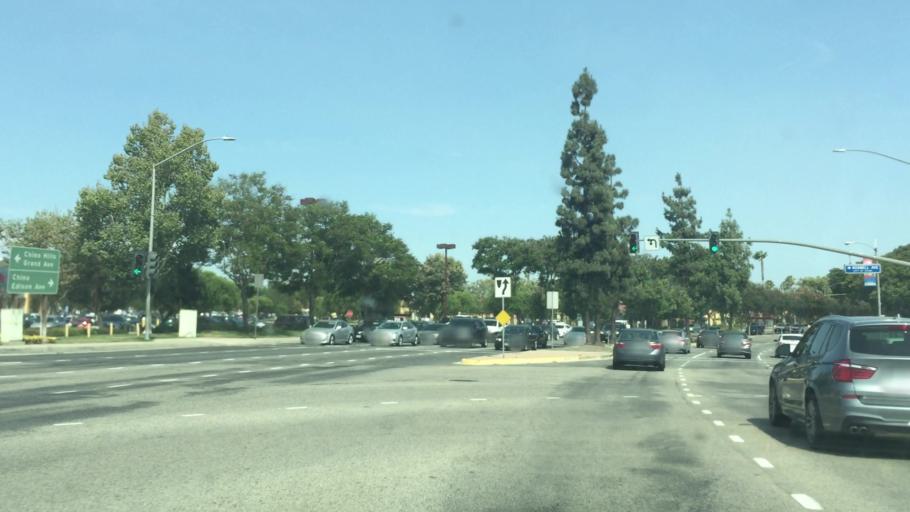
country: US
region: California
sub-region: San Bernardino County
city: Los Serranos
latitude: 34.0004
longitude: -117.7219
